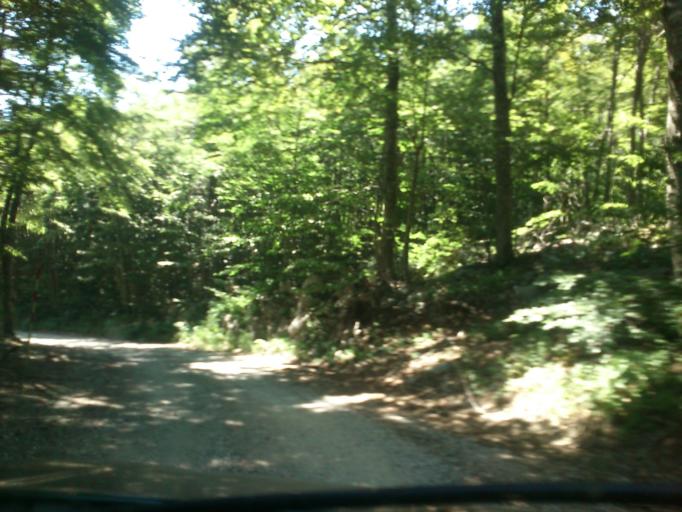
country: HR
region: Licko-Senjska
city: Senj
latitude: 44.8230
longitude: 14.9810
